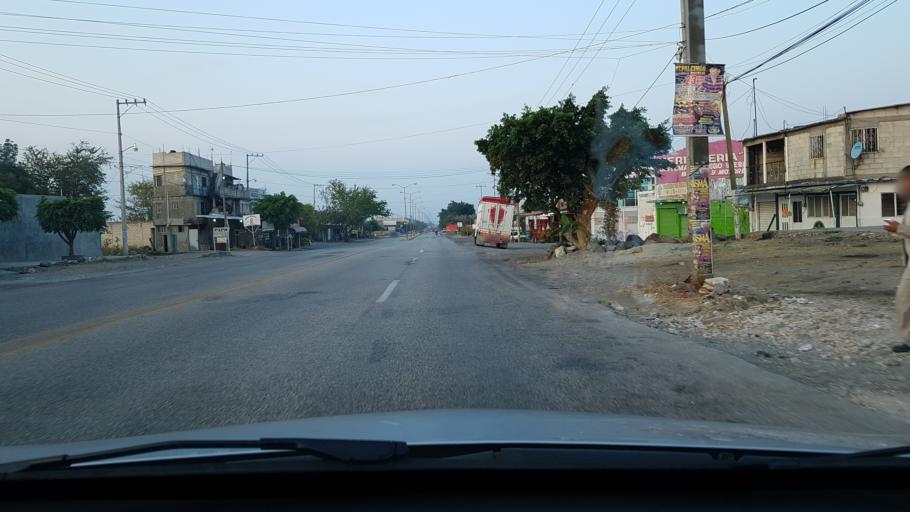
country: MX
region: Morelos
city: Amayuca
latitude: 18.7171
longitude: -98.7954
